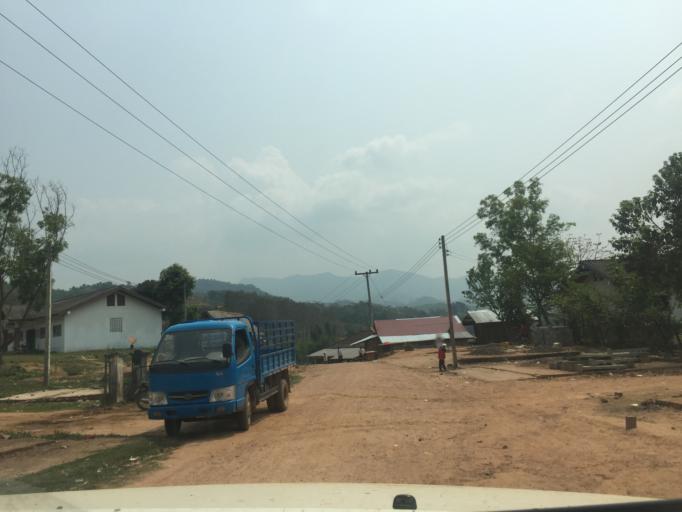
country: LA
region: Loungnamtha
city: Muang Nale
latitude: 20.2013
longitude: 101.6640
